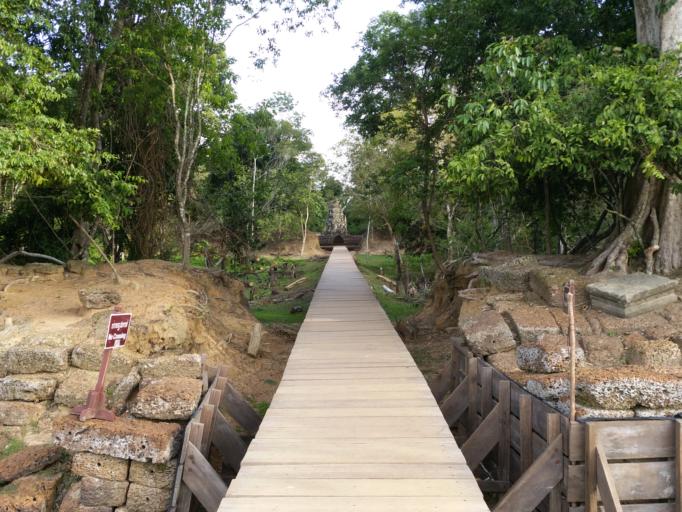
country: KH
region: Siem Reap
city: Siem Reap
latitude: 13.4648
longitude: 103.8948
